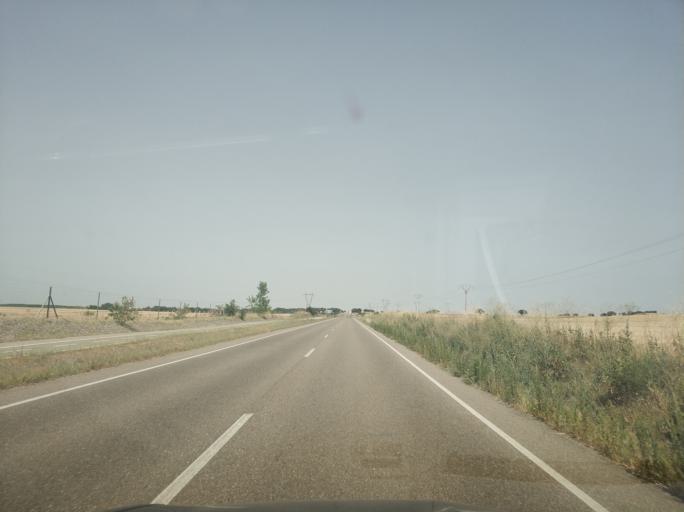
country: ES
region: Castille and Leon
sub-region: Provincia de Salamanca
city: Florida de Liebana
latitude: 41.0262
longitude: -5.7251
